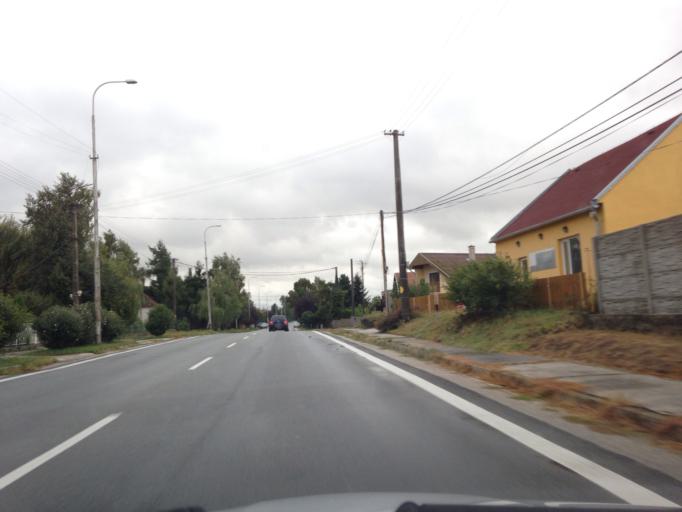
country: SK
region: Nitriansky
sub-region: Okres Komarno
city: Hurbanovo
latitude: 47.8515
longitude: 18.1721
